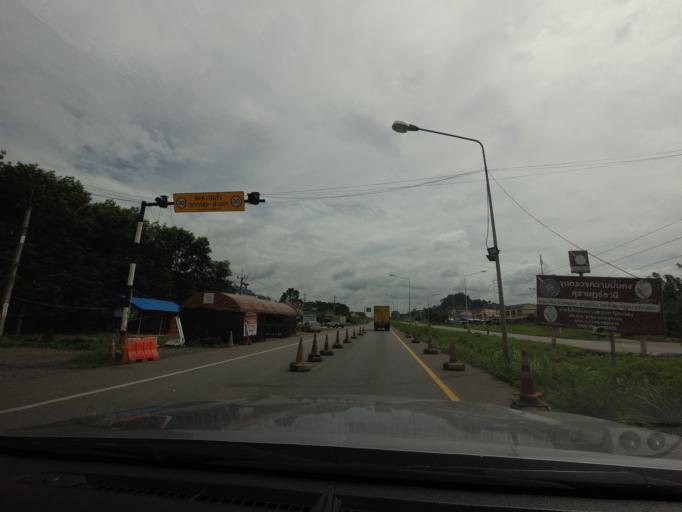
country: TH
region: Surat Thani
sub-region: Amphoe Wiang Sa
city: Wiang Sa
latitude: 8.5669
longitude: 99.3455
